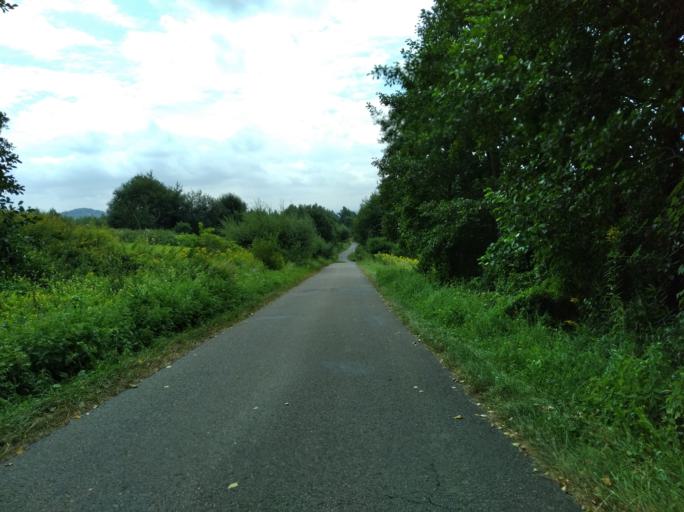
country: PL
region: Subcarpathian Voivodeship
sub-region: Powiat krosnienski
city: Leki
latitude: 49.8148
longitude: 21.6650
